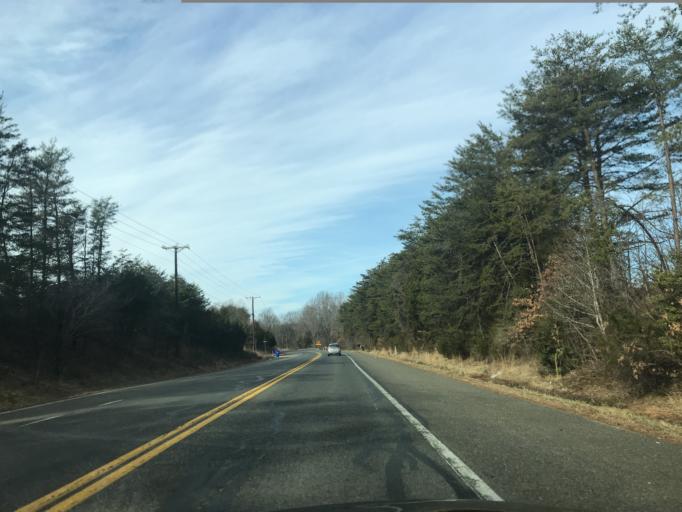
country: US
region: Maryland
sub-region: Charles County
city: Indian Head
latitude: 38.4856
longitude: -77.1166
